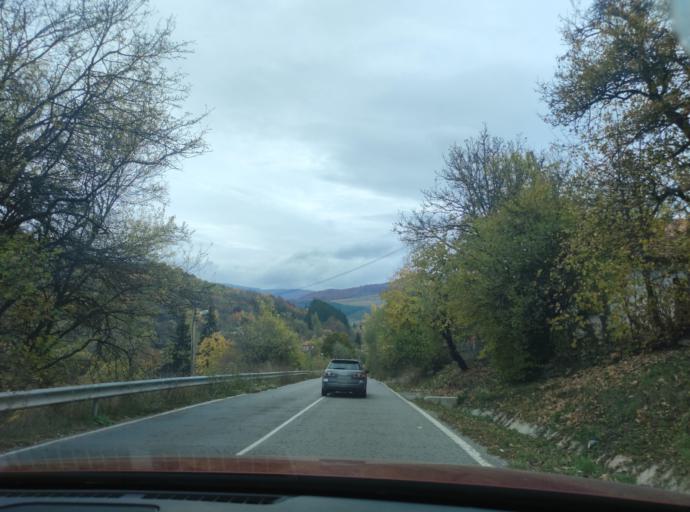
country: BG
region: Sofiya
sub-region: Obshtina Godech
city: Godech
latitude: 43.0669
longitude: 23.1079
